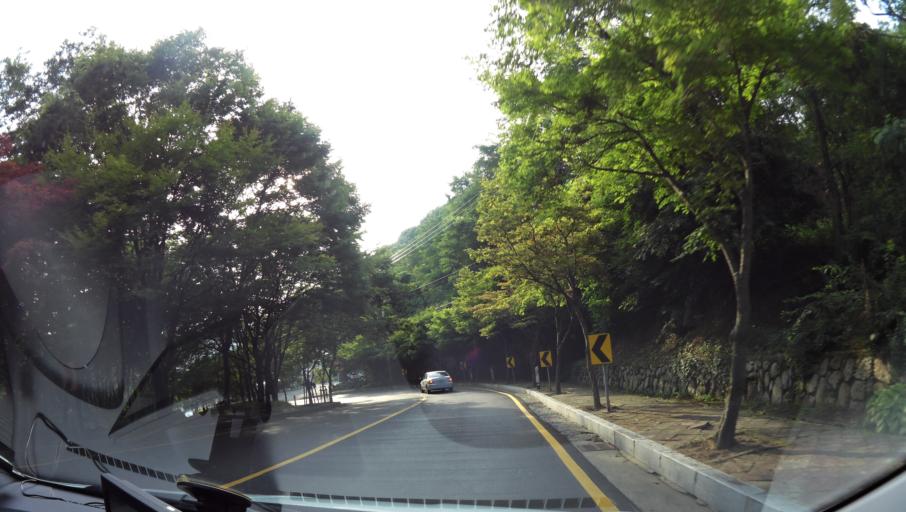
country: KR
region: Daegu
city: Daegu
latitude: 35.9855
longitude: 128.6590
